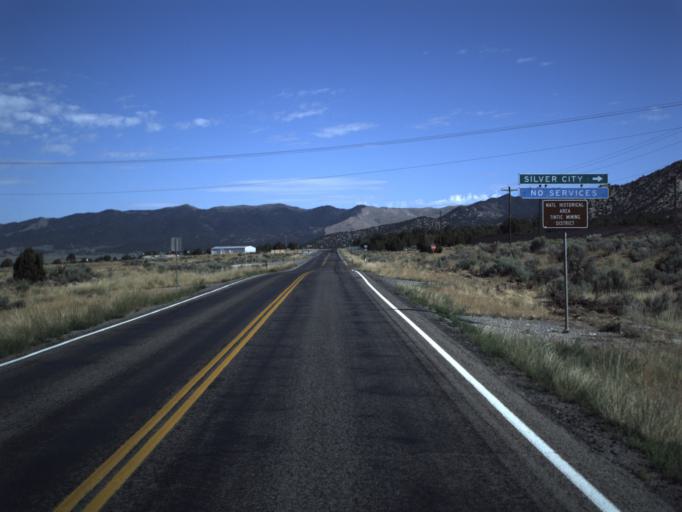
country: US
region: Utah
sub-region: Juab County
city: Mona
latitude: 39.9156
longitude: -112.1429
